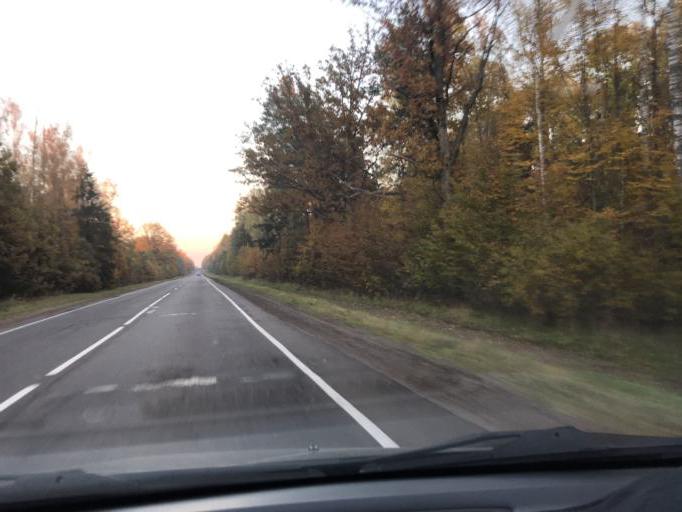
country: BY
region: Mogilev
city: Hlusha
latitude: 53.0897
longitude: 28.8917
